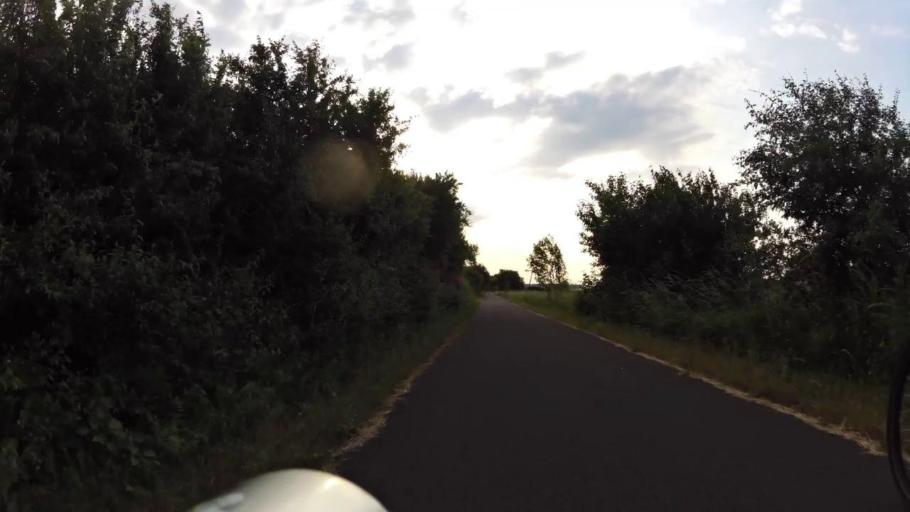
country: PL
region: Kujawsko-Pomorskie
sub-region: Powiat chelminski
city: Unislaw
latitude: 53.1818
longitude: 18.3987
